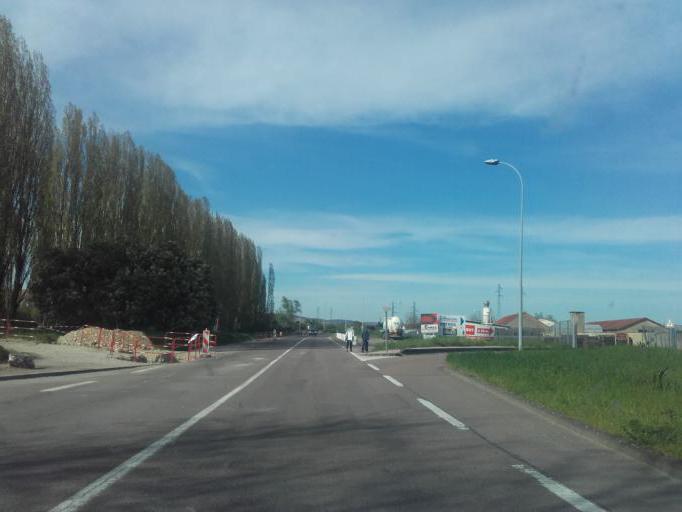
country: FR
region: Bourgogne
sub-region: Departement de la Cote-d'Or
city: Beaune
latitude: 47.0214
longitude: 4.8575
